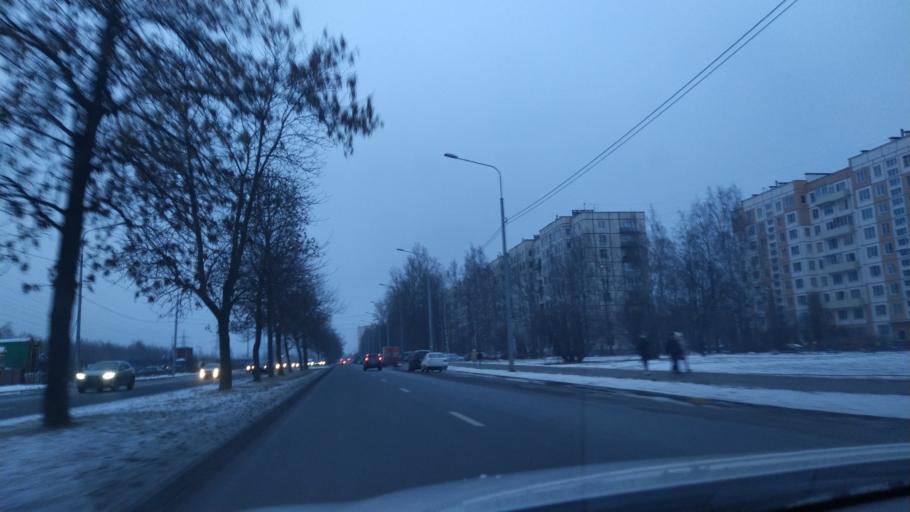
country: RU
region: St.-Petersburg
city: Grazhdanka
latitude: 60.0188
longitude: 30.4188
